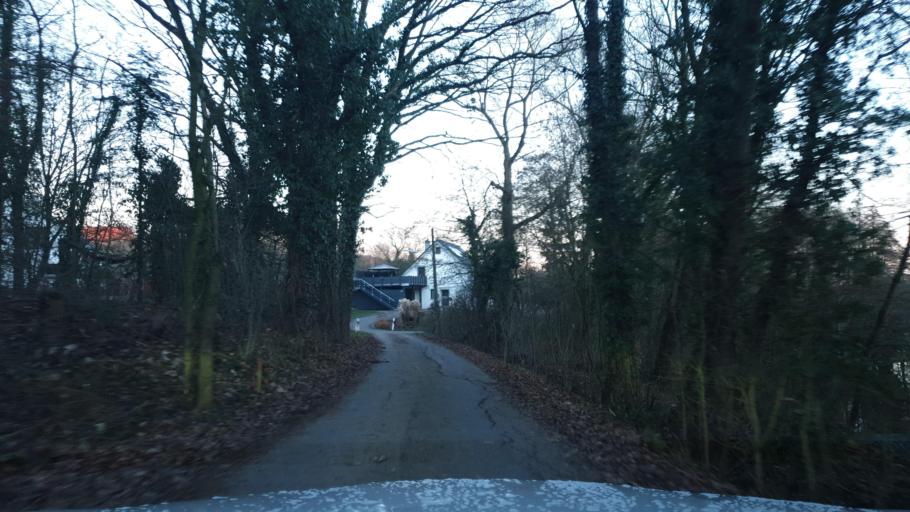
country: DE
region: North Rhine-Westphalia
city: Bad Oeynhausen
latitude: 52.2395
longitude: 8.8261
